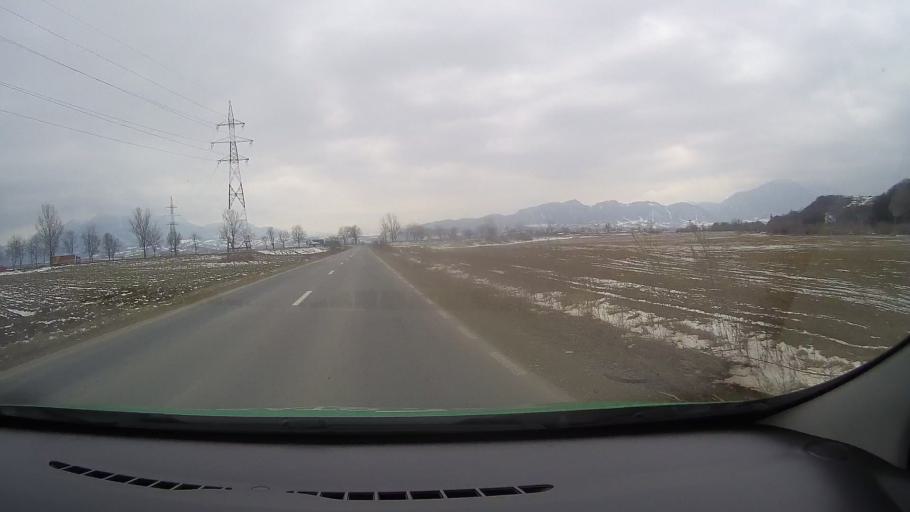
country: RO
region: Brasov
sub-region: Comuna Zarnesti
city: Tohanu Nou
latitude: 45.5824
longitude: 25.4066
